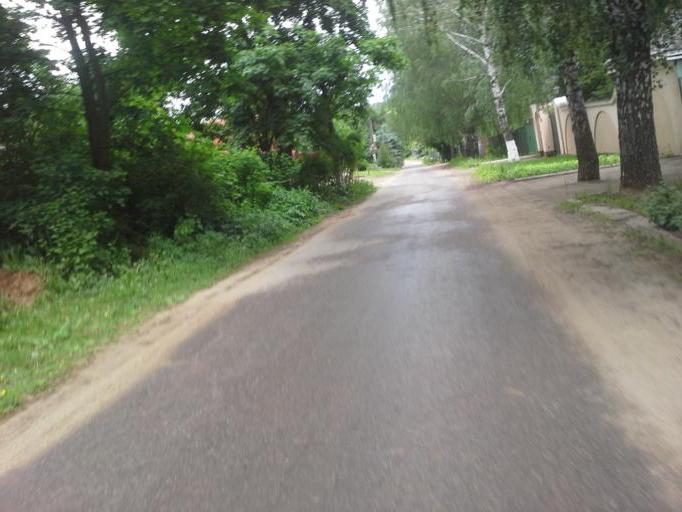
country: RU
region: Moskovskaya
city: Lesnoy Gorodok
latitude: 55.6348
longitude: 37.2295
